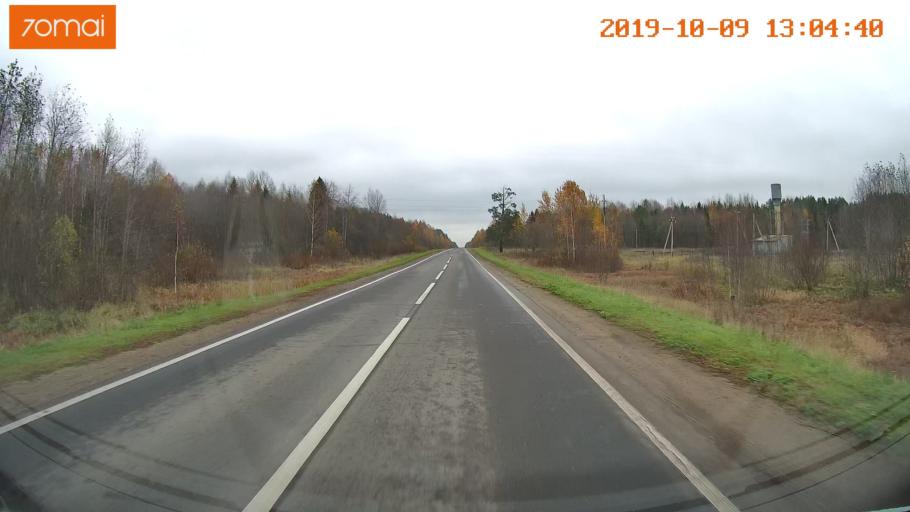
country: RU
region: Jaroslavl
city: Lyubim
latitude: 58.3582
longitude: 40.5602
